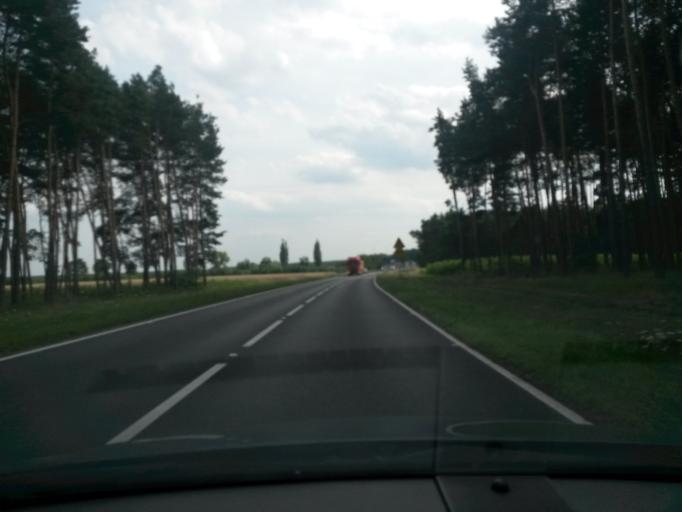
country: PL
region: Greater Poland Voivodeship
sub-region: Powiat poznanski
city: Kornik
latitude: 52.2216
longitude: 17.0737
